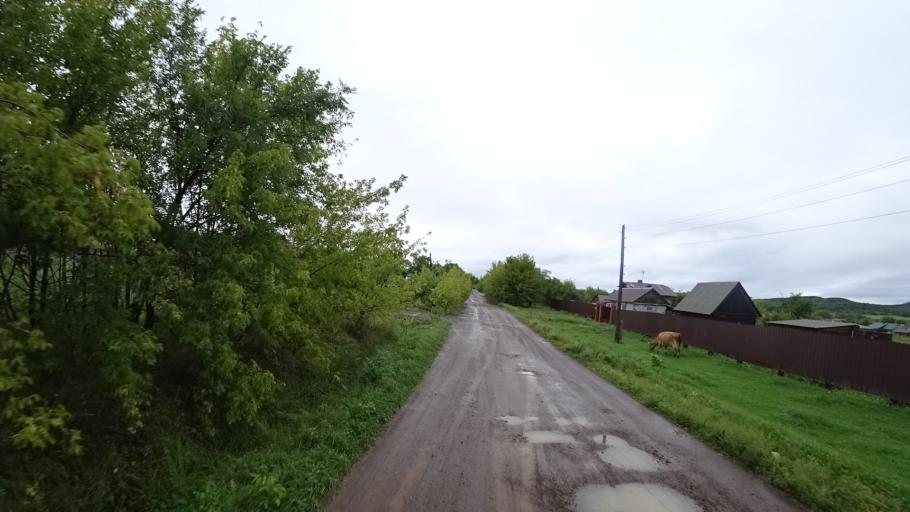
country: RU
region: Primorskiy
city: Monastyrishche
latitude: 44.2587
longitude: 132.4233
